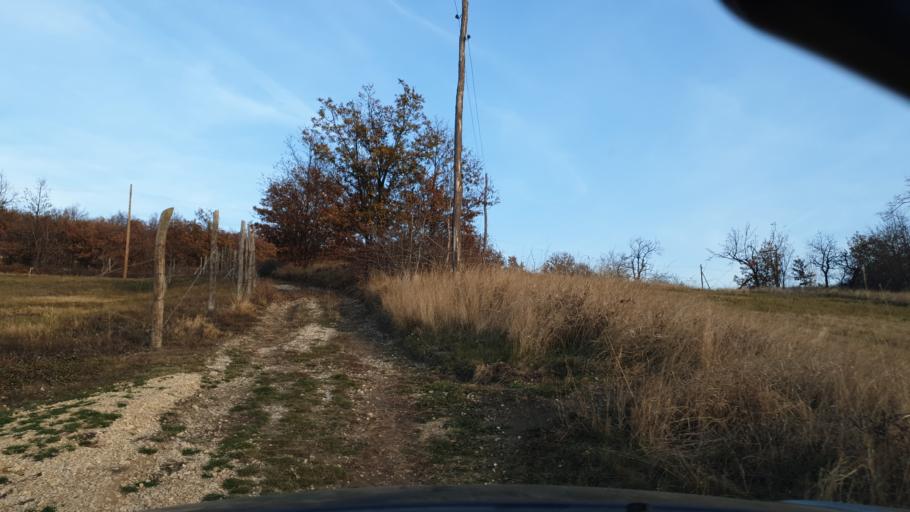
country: RS
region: Central Serbia
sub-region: Borski Okrug
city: Bor
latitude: 44.0650
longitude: 22.0806
